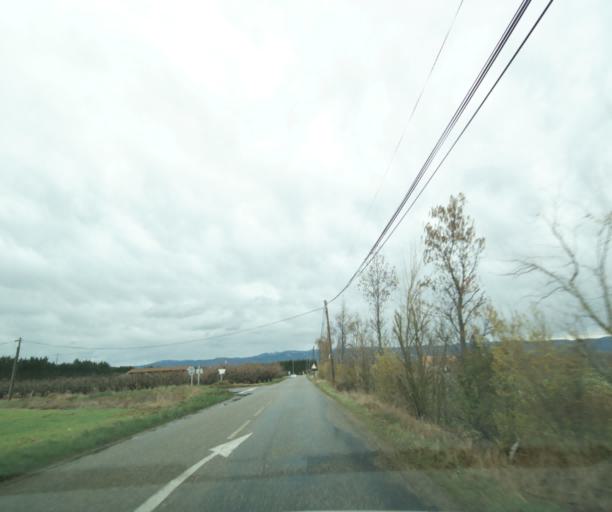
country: FR
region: Rhone-Alpes
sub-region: Departement de la Drome
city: Bourg-les-Valence
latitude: 44.9660
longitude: 4.9343
